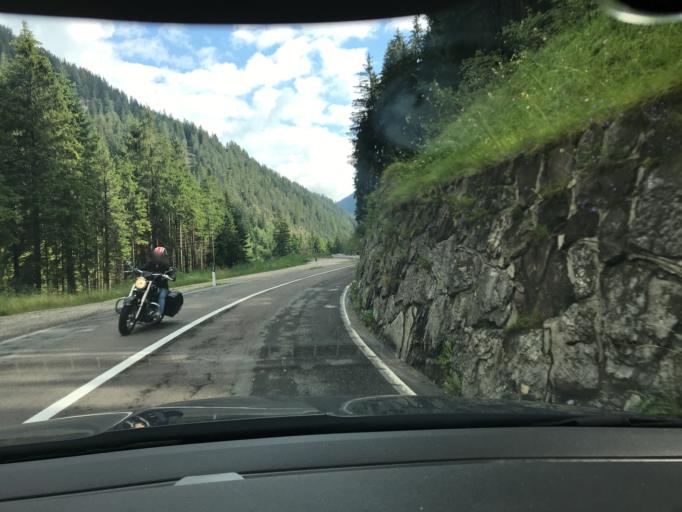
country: IT
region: Trentino-Alto Adige
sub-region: Bolzano
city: La Valle - Wengen
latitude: 46.6385
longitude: 11.9003
